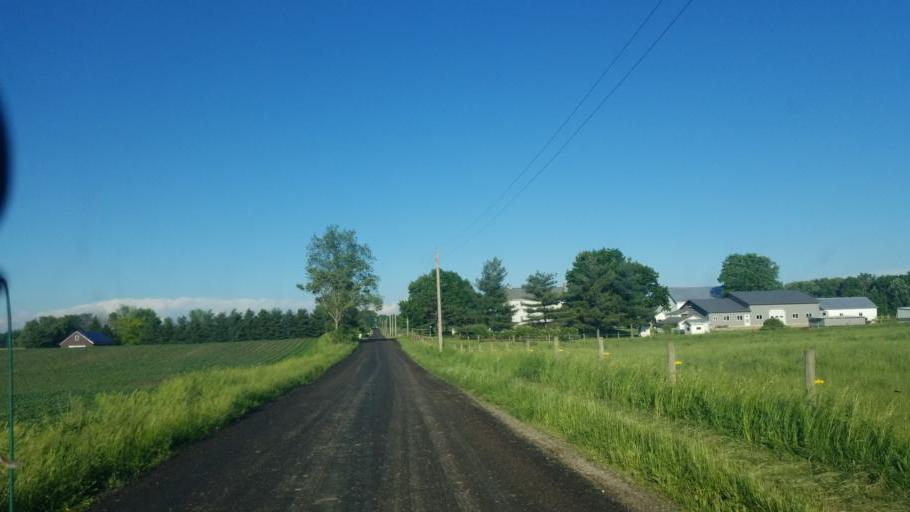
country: US
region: Indiana
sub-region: Marshall County
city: Bremen
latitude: 41.4192
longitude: -86.0827
